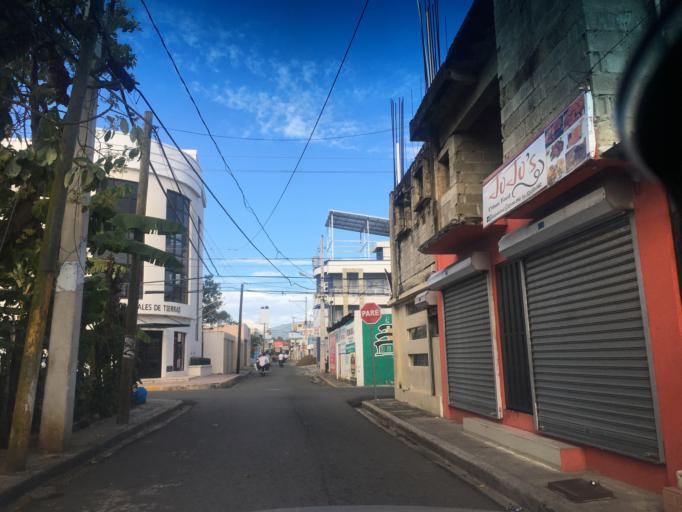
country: DO
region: Duarte
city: San Francisco de Macoris
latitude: 19.2988
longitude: -70.2603
